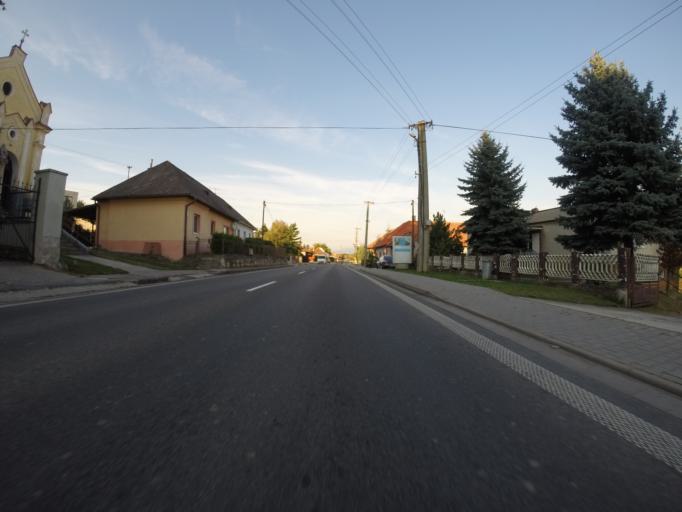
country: SK
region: Nitriansky
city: Banovce nad Bebravou
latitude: 48.5928
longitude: 18.2072
